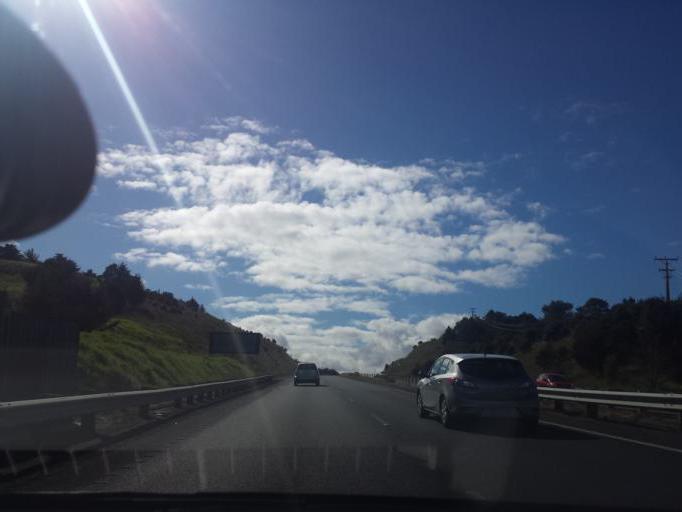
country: NZ
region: Auckland
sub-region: Auckland
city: Rothesay Bay
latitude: -36.5978
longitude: 174.6625
